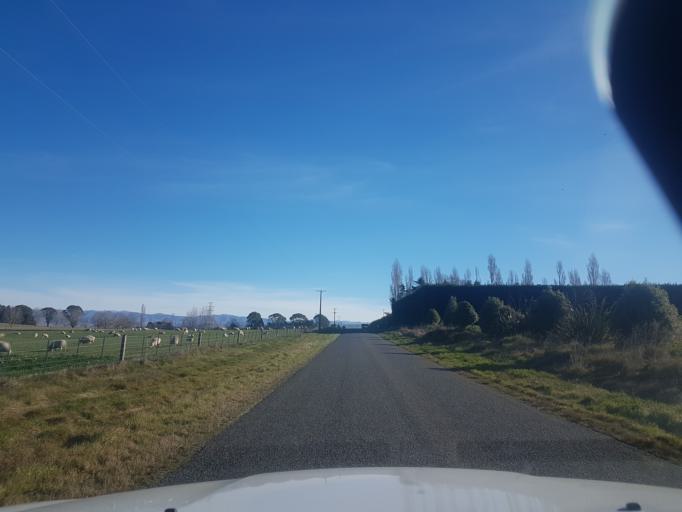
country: NZ
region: Canterbury
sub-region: Timaru District
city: Pleasant Point
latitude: -44.2518
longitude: 171.0557
